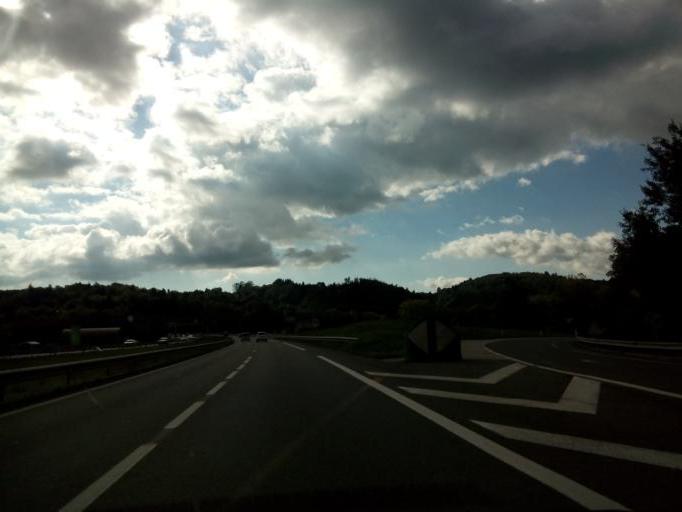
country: FR
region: Rhone-Alpes
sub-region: Departement de la Savoie
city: Novalaise
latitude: 45.5797
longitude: 5.8010
